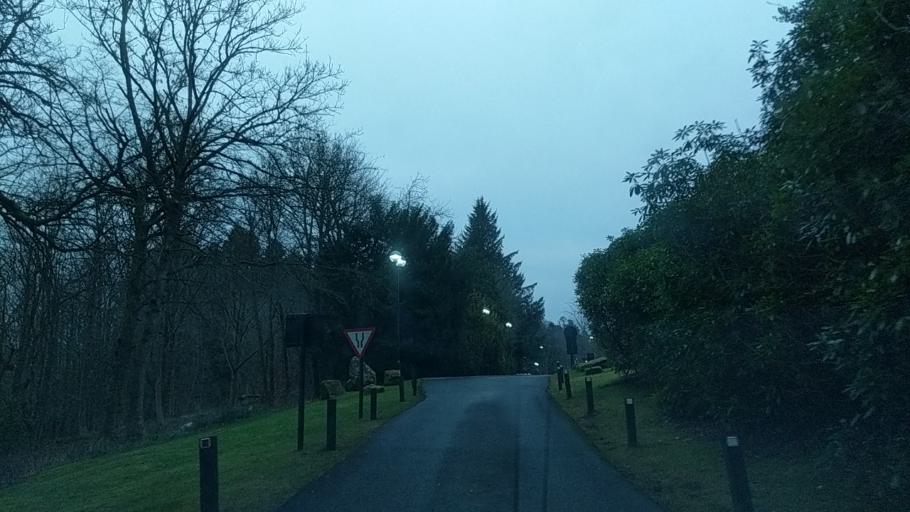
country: GB
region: Scotland
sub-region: South Lanarkshire
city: East Kilbride
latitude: 55.7396
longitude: -4.1488
